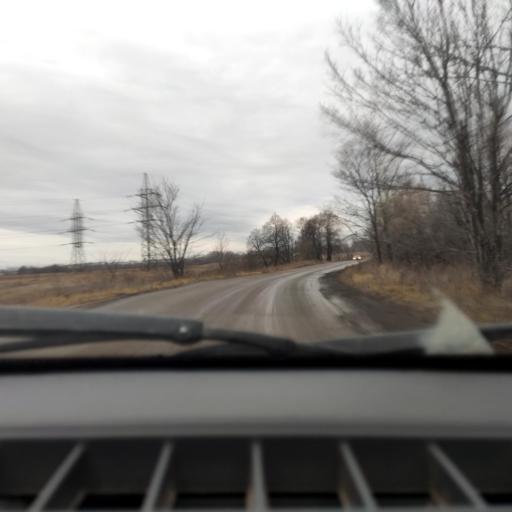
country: RU
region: Bashkortostan
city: Blagoveshchensk
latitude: 54.9399
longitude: 56.0990
